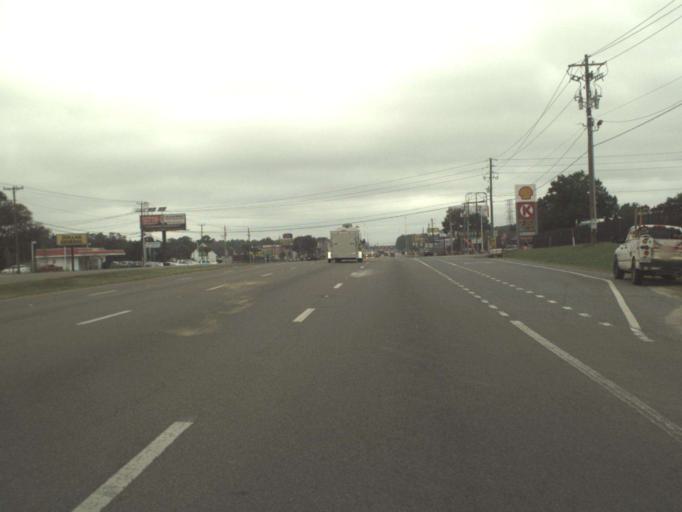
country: US
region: Florida
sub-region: Escambia County
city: Brent
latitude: 30.4894
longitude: -87.2597
